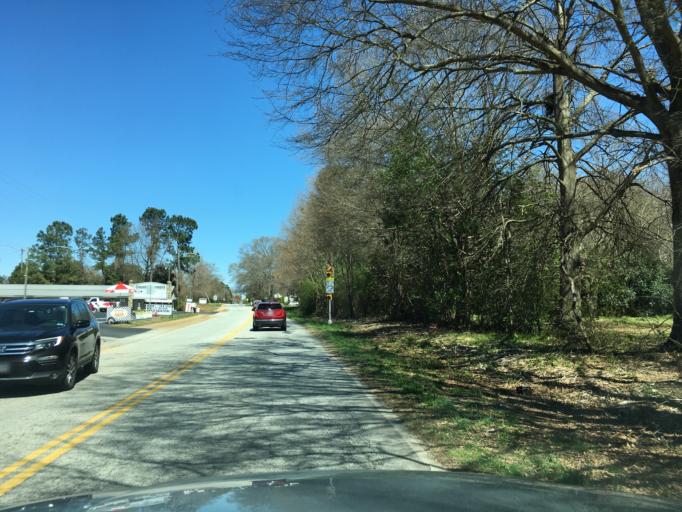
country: US
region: South Carolina
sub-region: Spartanburg County
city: Fairforest
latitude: 34.9235
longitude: -82.0016
